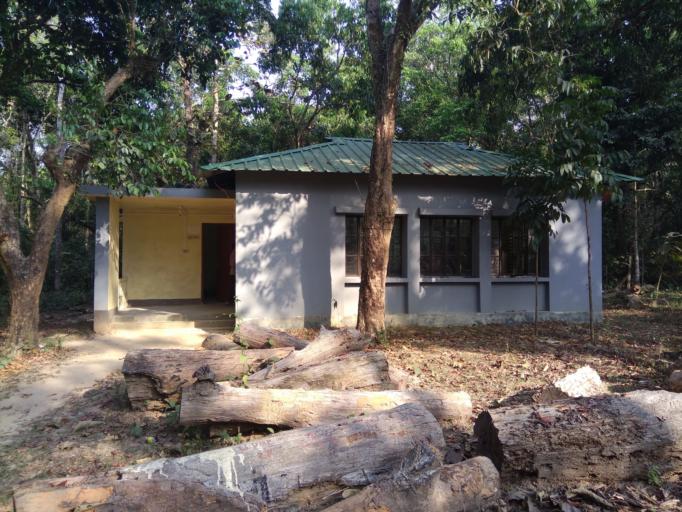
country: BD
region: Chittagong
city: Cox's Bazar
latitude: 21.6789
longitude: 92.0781
